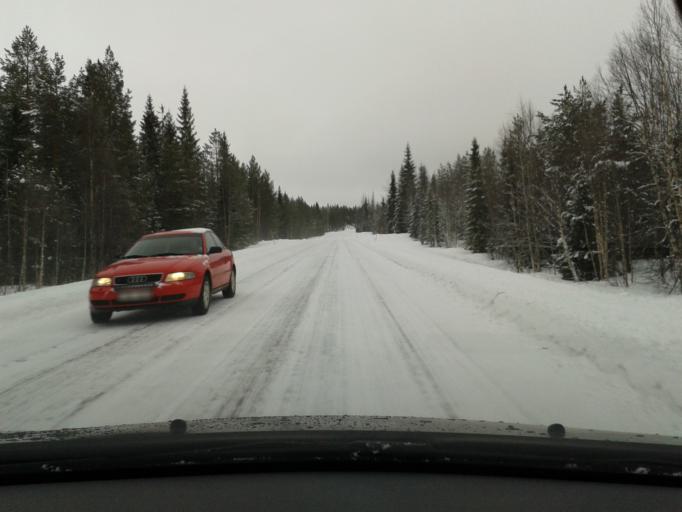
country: SE
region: Vaesterbotten
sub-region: Vilhelmina Kommun
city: Sjoberg
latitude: 64.8719
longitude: 15.8868
